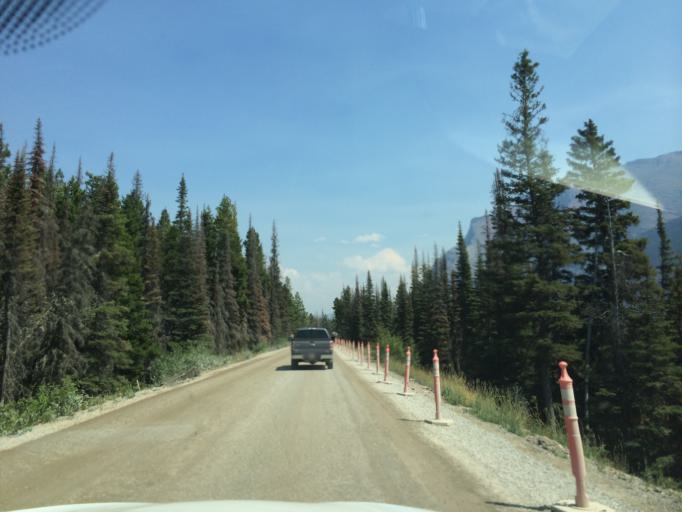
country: US
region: Montana
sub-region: Glacier County
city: Browning
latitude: 48.6755
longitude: -113.6024
